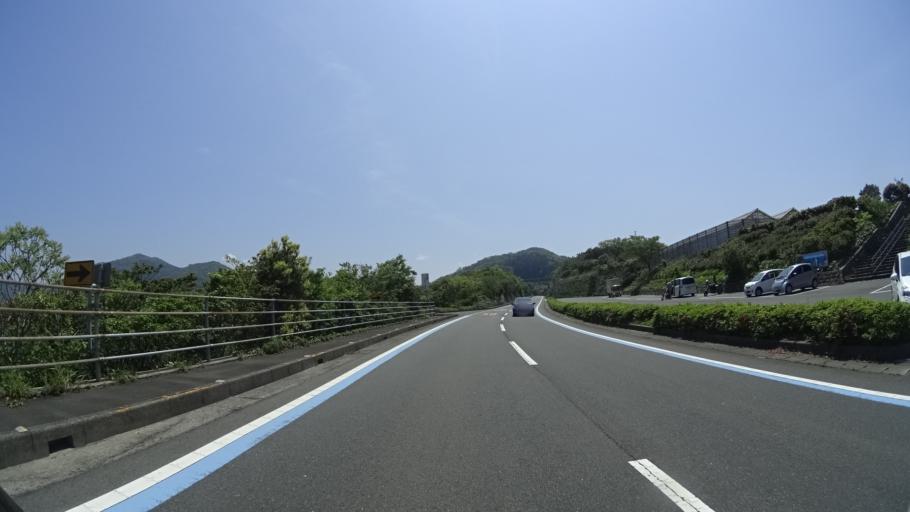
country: JP
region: Ehime
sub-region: Nishiuwa-gun
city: Ikata-cho
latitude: 33.4480
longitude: 132.2582
